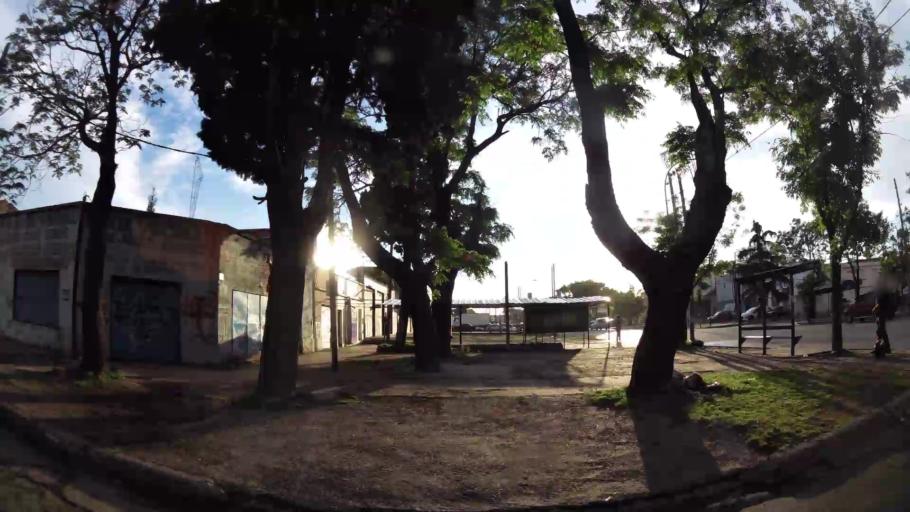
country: AR
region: Buenos Aires
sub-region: Partido de Almirante Brown
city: Adrogue
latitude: -34.7605
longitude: -58.3591
